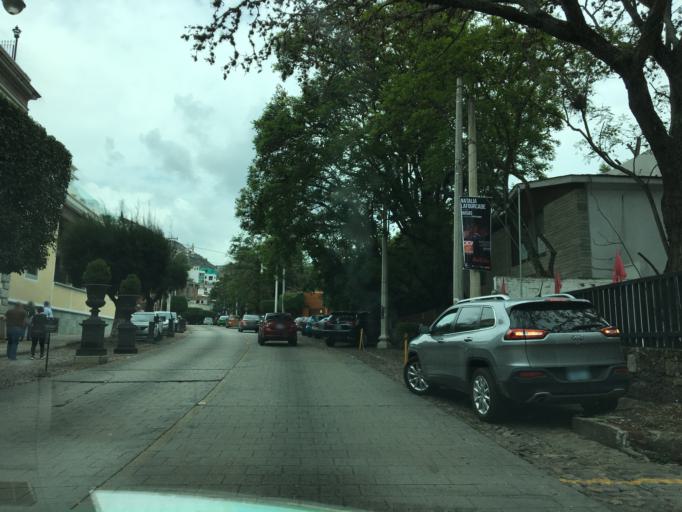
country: MX
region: Guanajuato
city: Guanajuato
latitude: 21.0043
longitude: -101.2469
